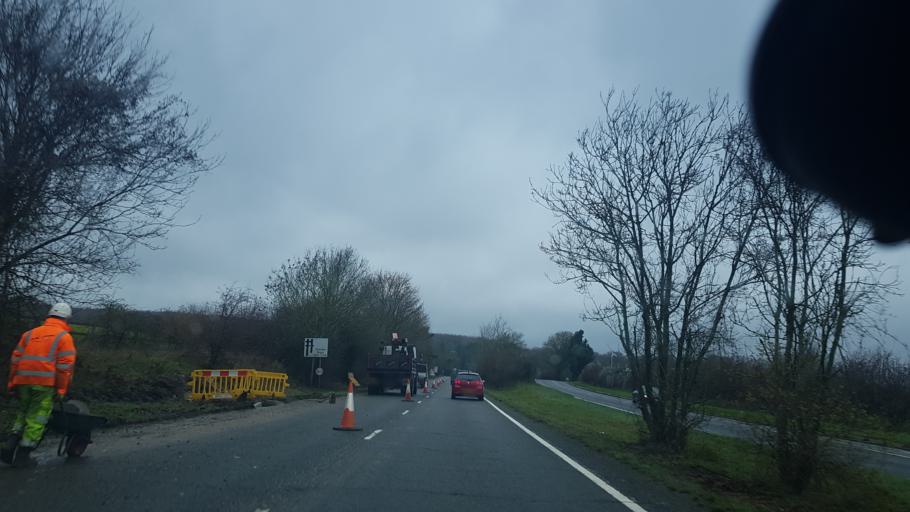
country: GB
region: England
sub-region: Surrey
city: Ripley
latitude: 51.2508
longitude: -0.4963
